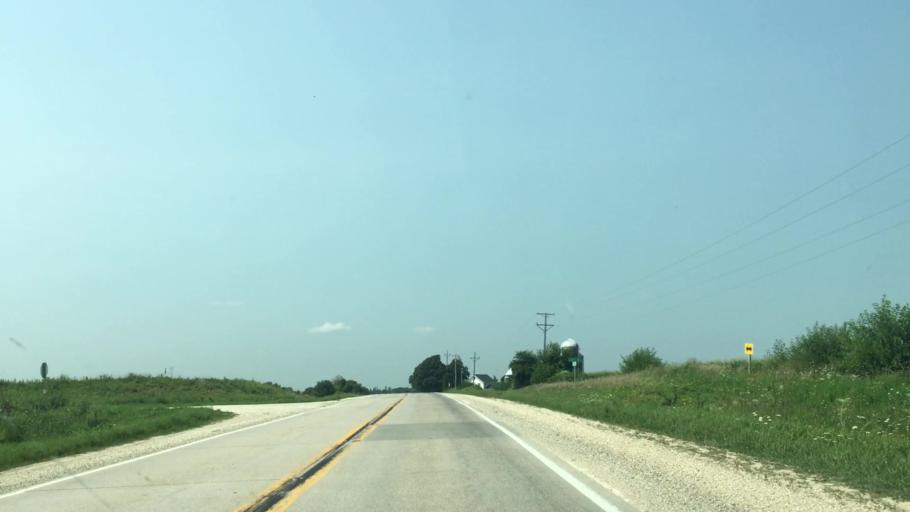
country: US
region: Iowa
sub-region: Fayette County
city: West Union
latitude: 43.0897
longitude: -91.8529
